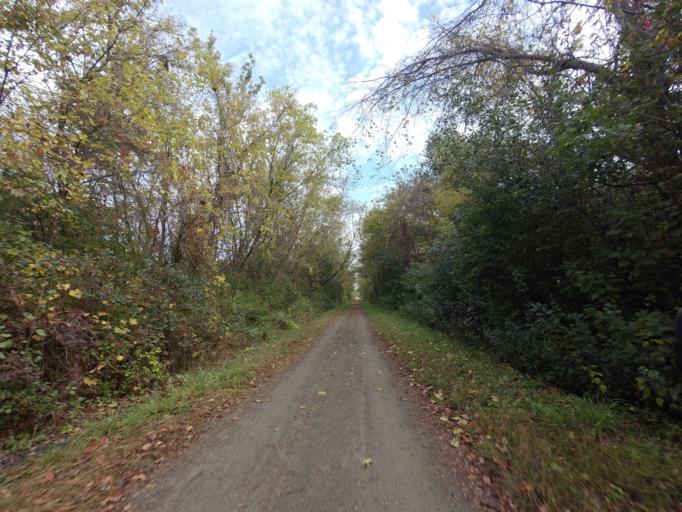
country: CA
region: Ontario
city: Ancaster
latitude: 43.2059
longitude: -80.0986
